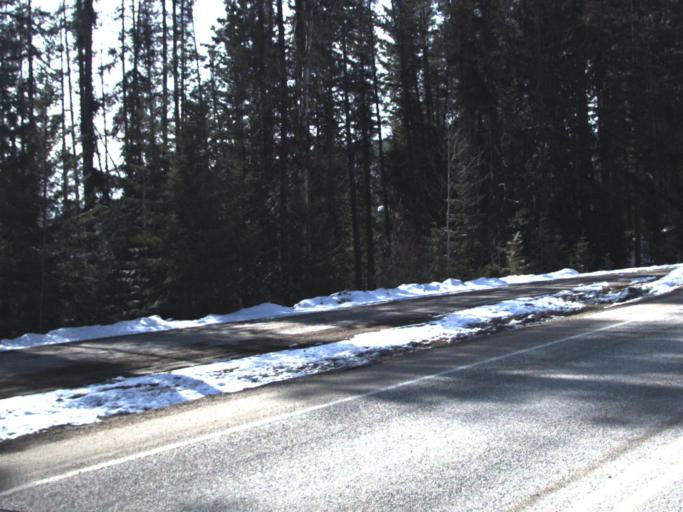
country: CA
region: British Columbia
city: Fruitvale
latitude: 48.6812
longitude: -117.4328
